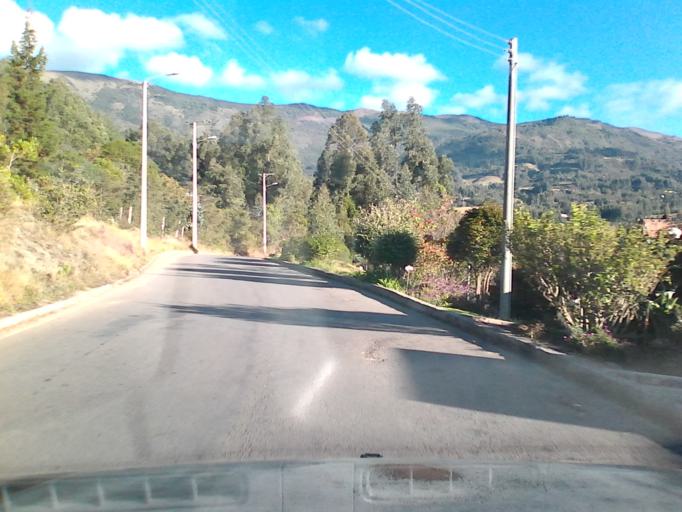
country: CO
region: Boyaca
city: Duitama
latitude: 5.8607
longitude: -73.0264
